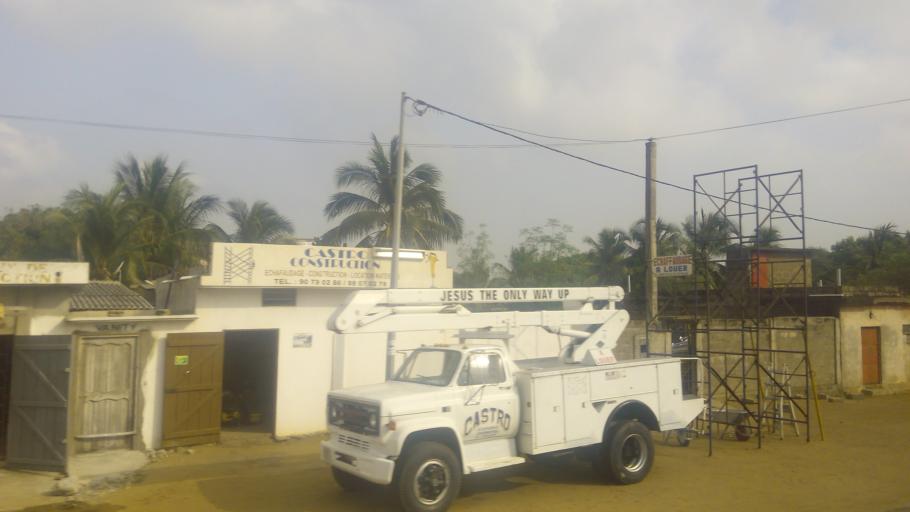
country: TG
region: Maritime
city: Lome
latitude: 6.1737
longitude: 1.3581
